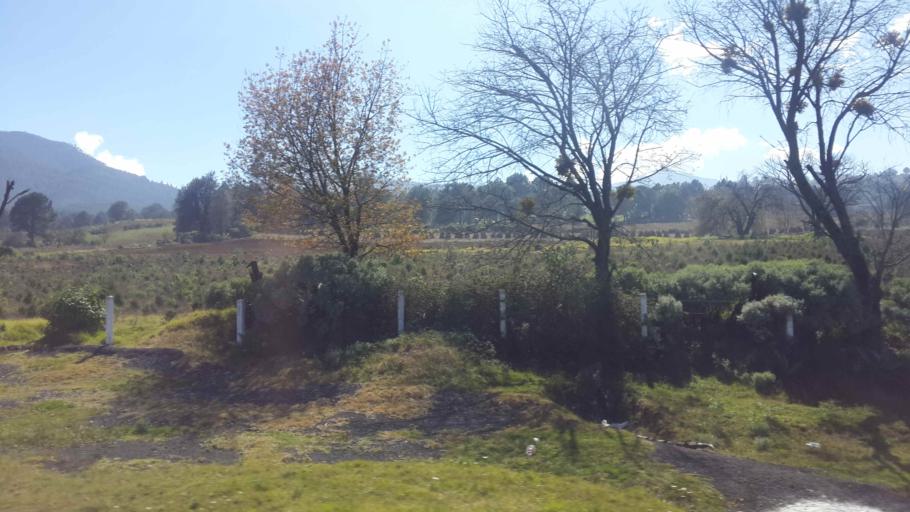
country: MX
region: Veracruz
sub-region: Las Vigas de Ramirez
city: Barrio de San Miguel
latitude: 19.6305
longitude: -97.1253
